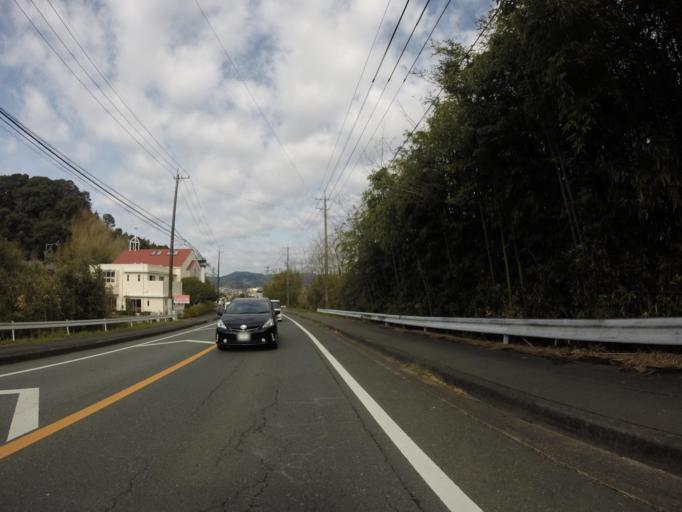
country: JP
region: Shizuoka
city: Hamakita
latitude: 34.8054
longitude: 137.6917
